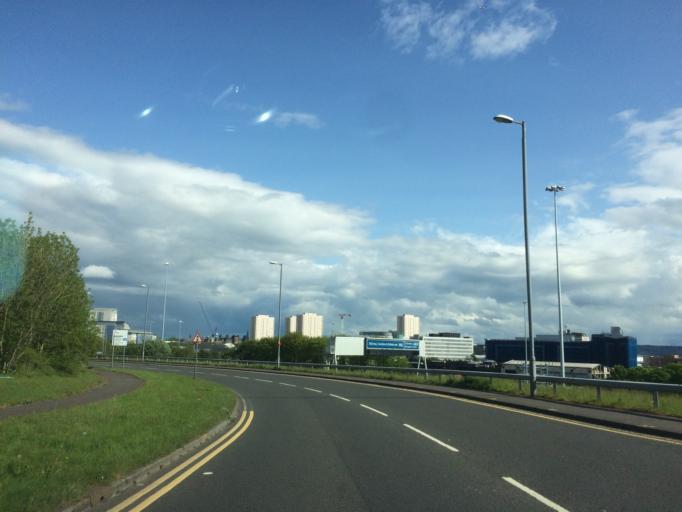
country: GB
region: Scotland
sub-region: Glasgow City
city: Glasgow
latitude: 55.8714
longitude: -4.2568
